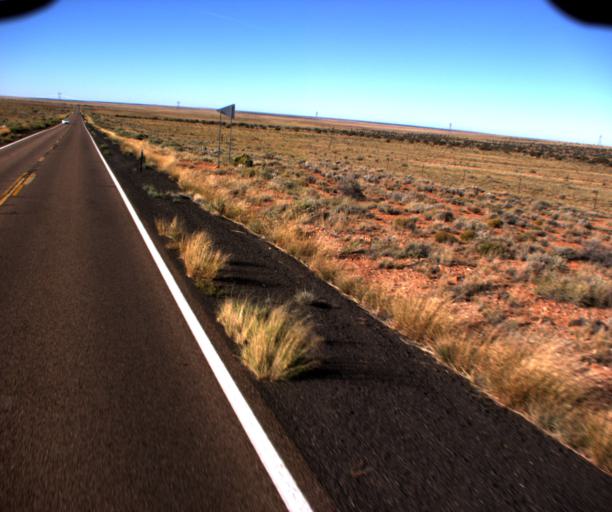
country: US
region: Arizona
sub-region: Navajo County
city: Holbrook
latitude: 34.8114
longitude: -110.2022
